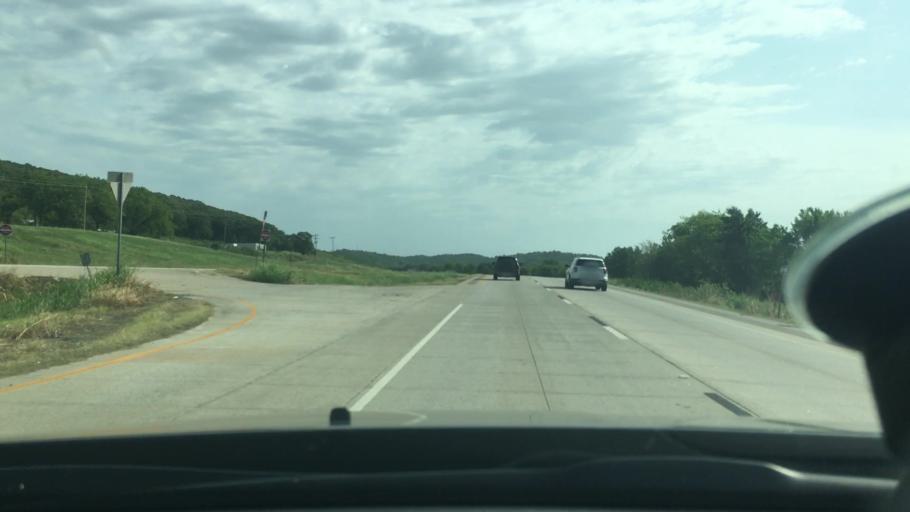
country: US
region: Oklahoma
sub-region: Atoka County
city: Atoka
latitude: 34.4328
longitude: -96.0803
